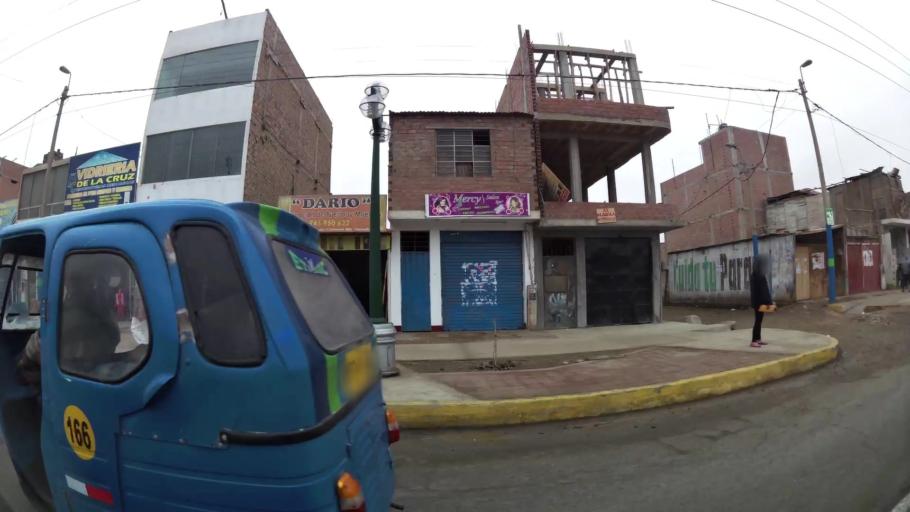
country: PE
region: Lima
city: Ventanilla
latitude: -11.8780
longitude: -77.1326
